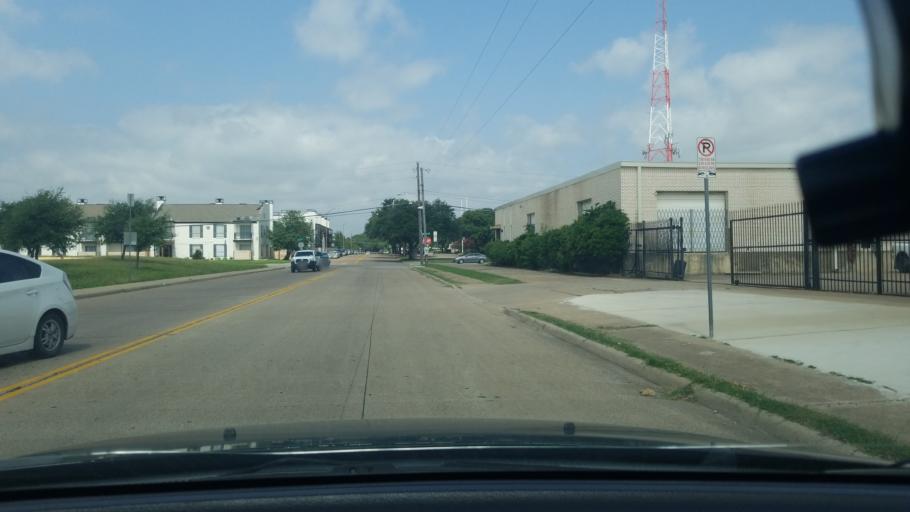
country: US
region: Texas
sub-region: Dallas County
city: Mesquite
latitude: 32.8028
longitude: -96.6872
